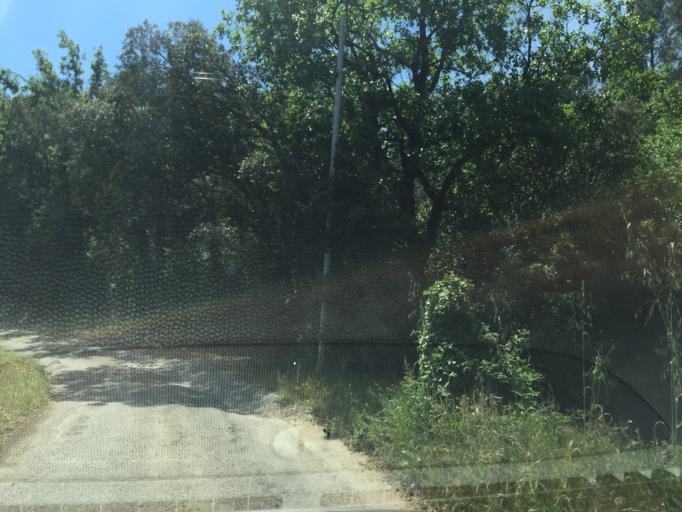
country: FR
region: Provence-Alpes-Cote d'Azur
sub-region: Departement du Var
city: Lorgues
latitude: 43.4771
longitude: 6.3679
